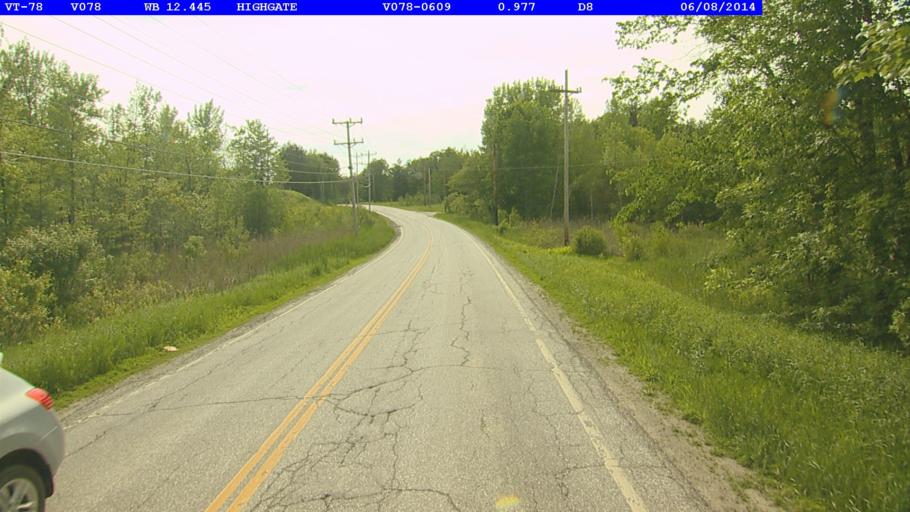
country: US
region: Vermont
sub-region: Franklin County
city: Swanton
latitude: 44.9335
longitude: -73.0819
